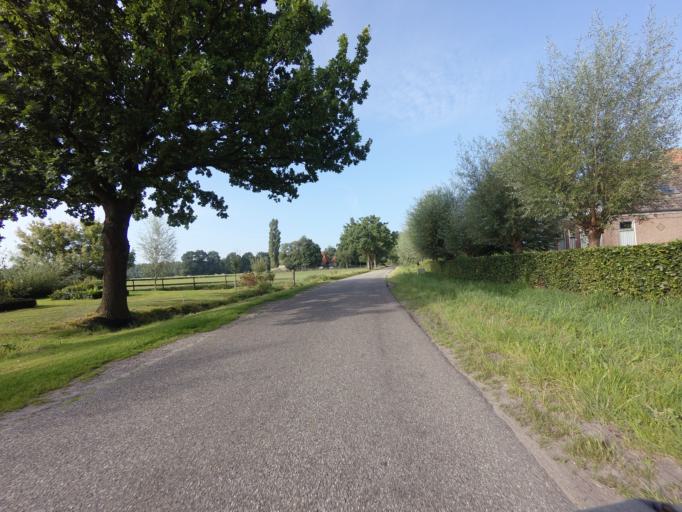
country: NL
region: Friesland
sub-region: Gemeente Weststellingwerf
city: Noordwolde
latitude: 52.9138
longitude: 6.1567
